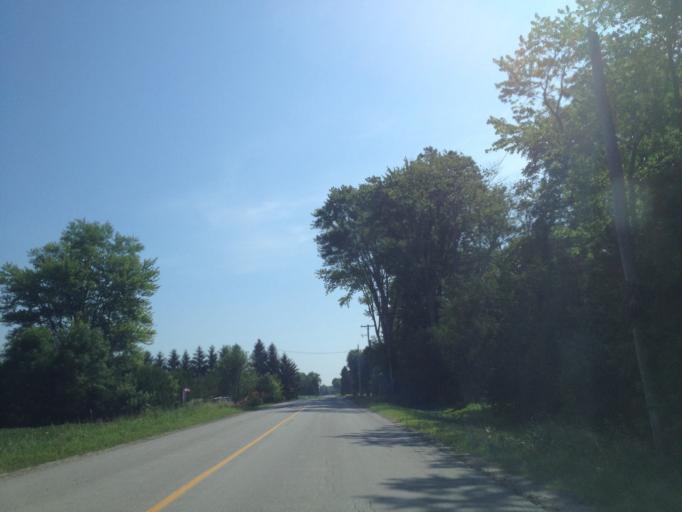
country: CA
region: Ontario
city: London
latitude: 43.1264
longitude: -81.2200
